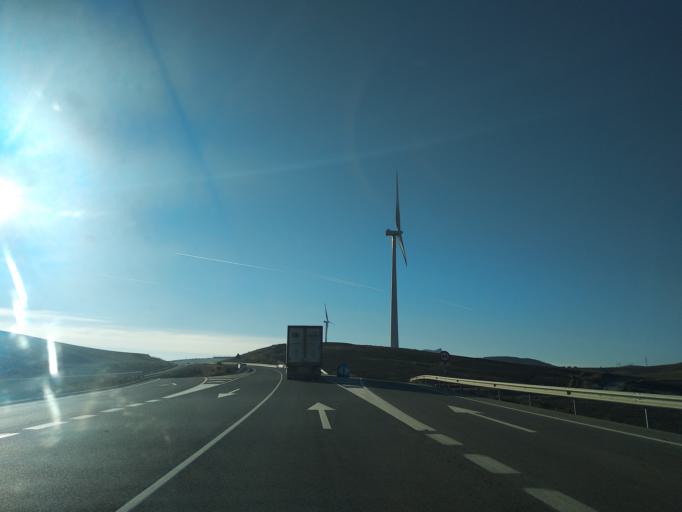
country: ES
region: Andalusia
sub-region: Provincia de Malaga
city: Ardales
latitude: 36.9407
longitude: -4.8668
